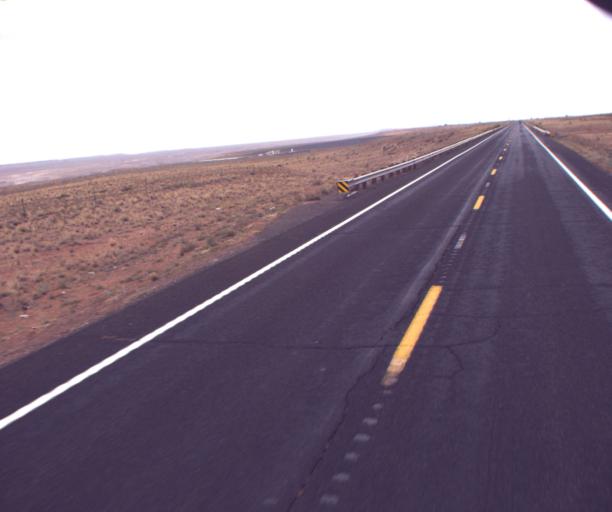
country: US
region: Arizona
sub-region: Coconino County
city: Tuba City
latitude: 36.1559
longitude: -111.1194
